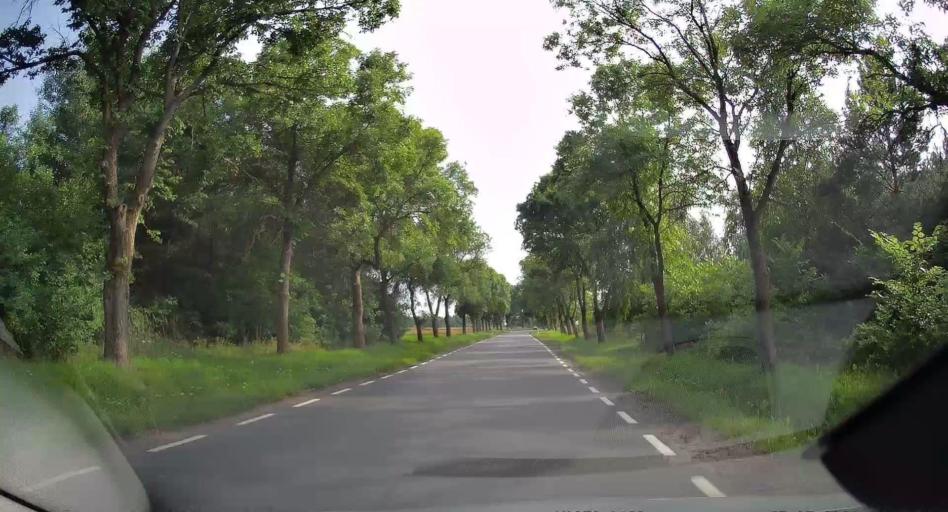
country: PL
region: Lodz Voivodeship
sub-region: Powiat tomaszowski
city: Inowlodz
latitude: 51.5370
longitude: 20.2319
